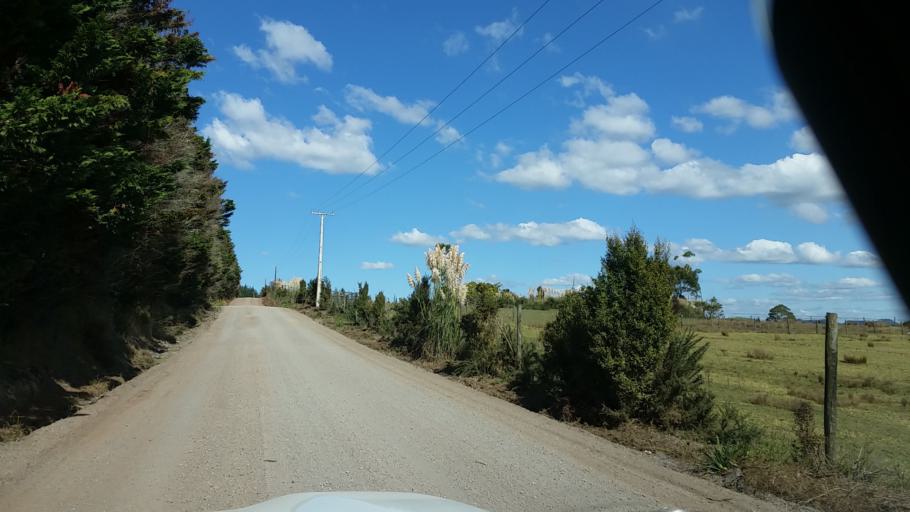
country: NZ
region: Northland
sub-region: Whangarei
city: Whangarei
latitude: -35.5818
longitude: 174.3110
